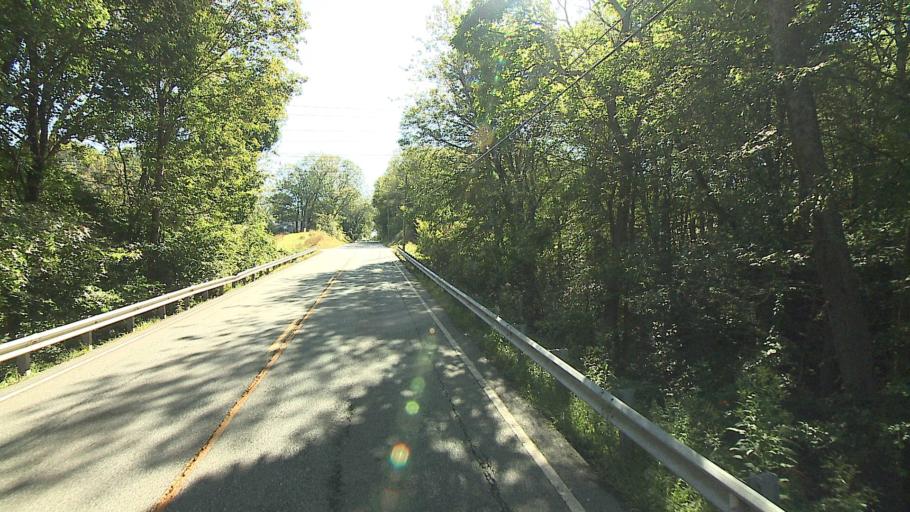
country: US
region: Connecticut
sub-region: New London County
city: Norwich
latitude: 41.5575
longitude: -72.0405
